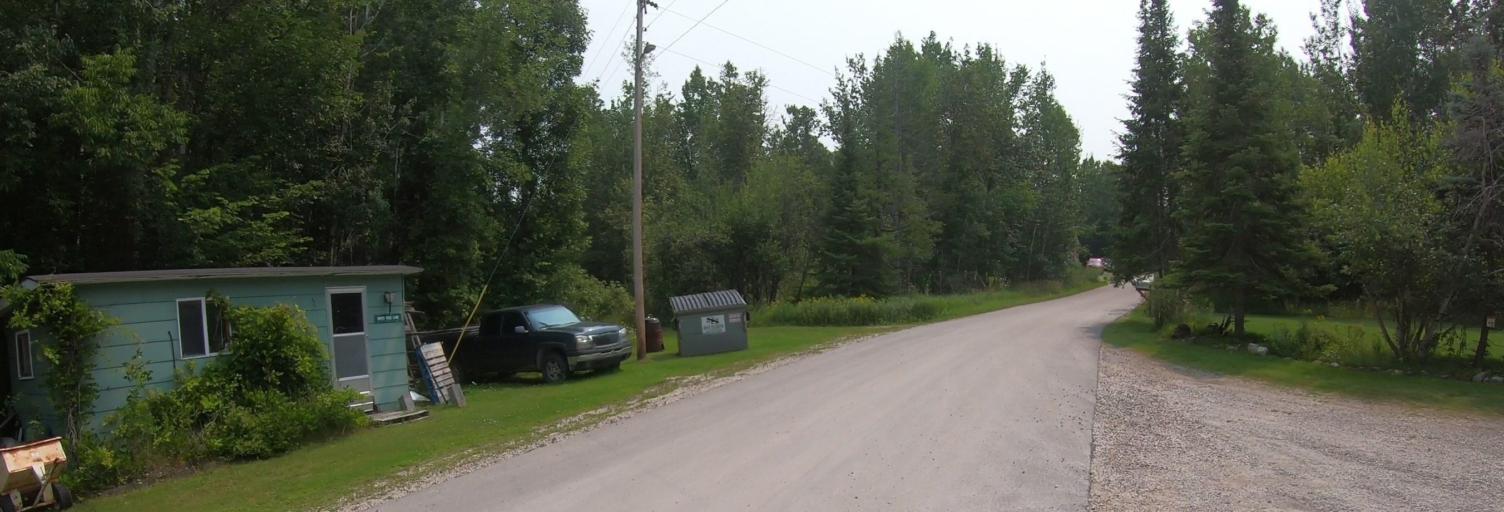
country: CA
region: Ontario
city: Thessalon
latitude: 46.0341
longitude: -83.6788
